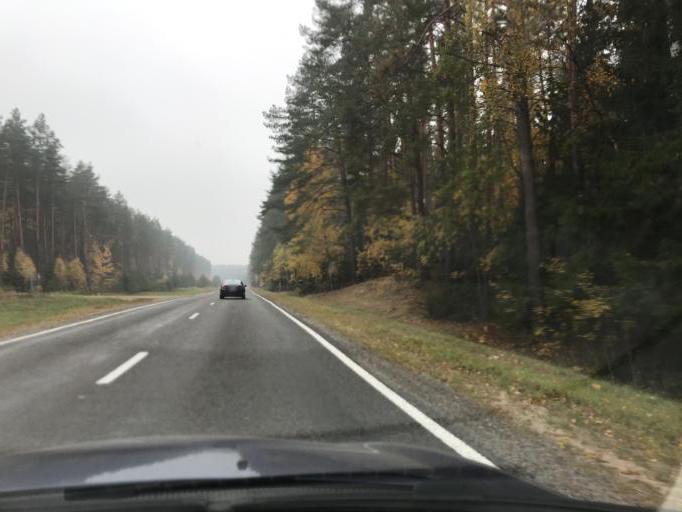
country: LT
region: Alytaus apskritis
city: Druskininkai
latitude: 53.8766
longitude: 23.8999
